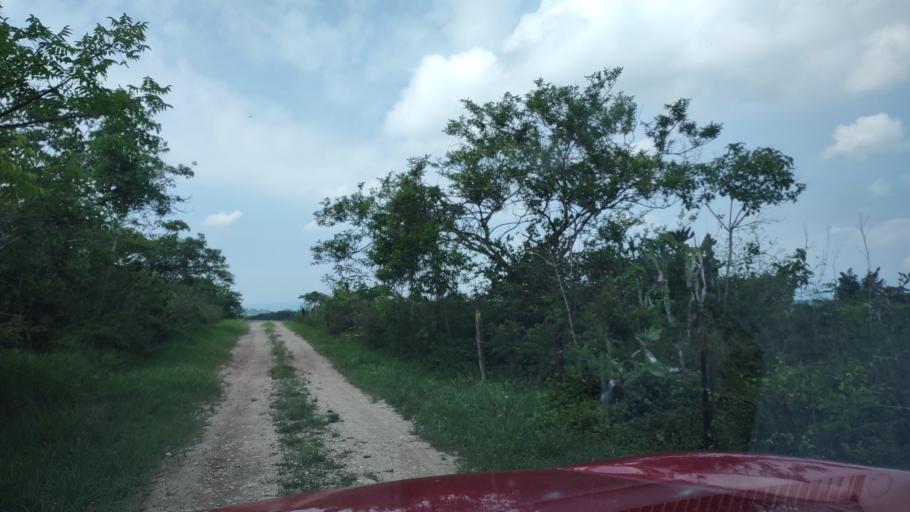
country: MX
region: Veracruz
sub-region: Emiliano Zapata
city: Dos Rios
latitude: 19.4499
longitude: -96.8093
